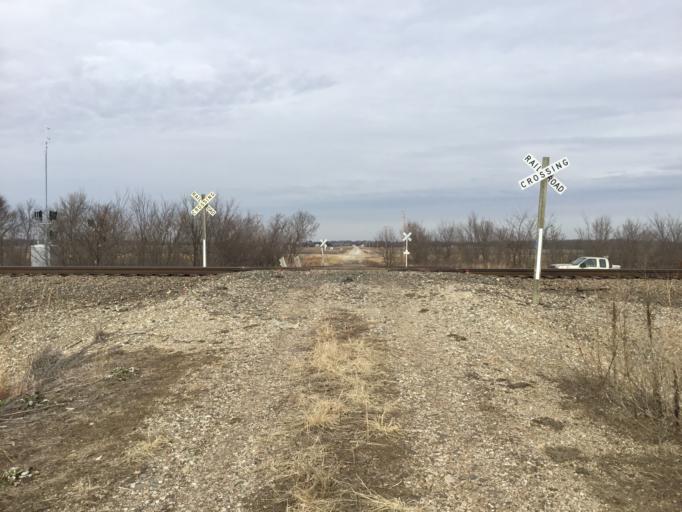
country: US
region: Kansas
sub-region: Chase County
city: Cottonwood Falls
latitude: 38.4052
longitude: -96.3733
